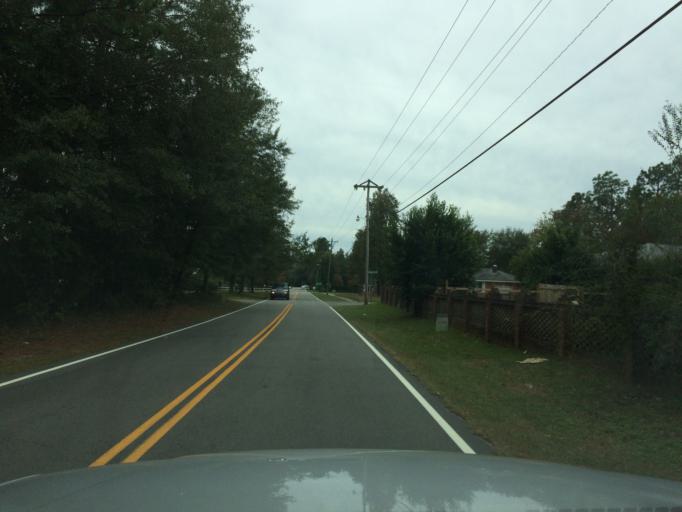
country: US
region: South Carolina
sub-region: Aiken County
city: New Ellenton
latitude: 33.4241
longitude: -81.6902
